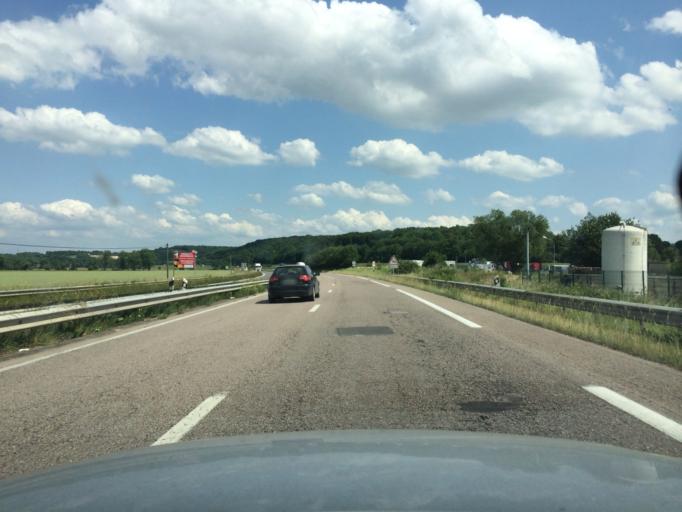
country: FR
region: Lorraine
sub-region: Departement de la Meuse
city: Vacon
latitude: 48.6872
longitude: 5.6320
